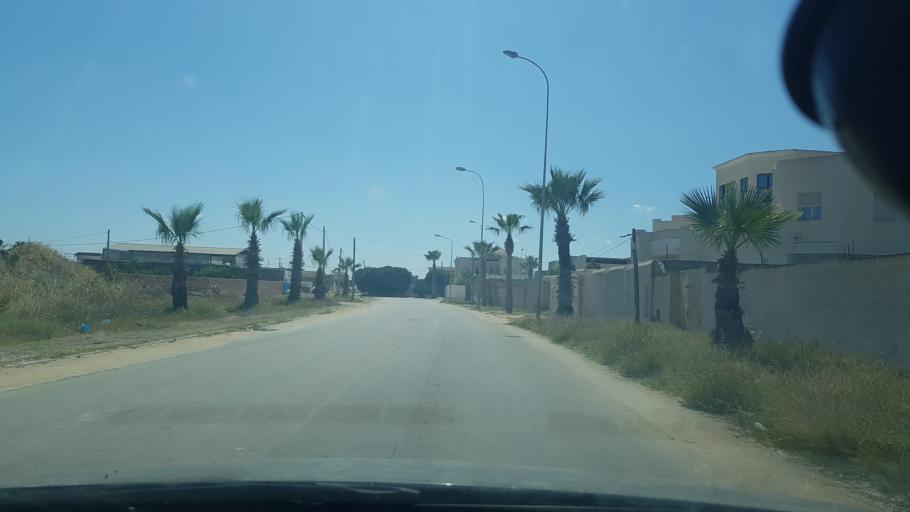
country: TN
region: Safaqis
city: Al Qarmadah
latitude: 34.8243
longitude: 10.7597
